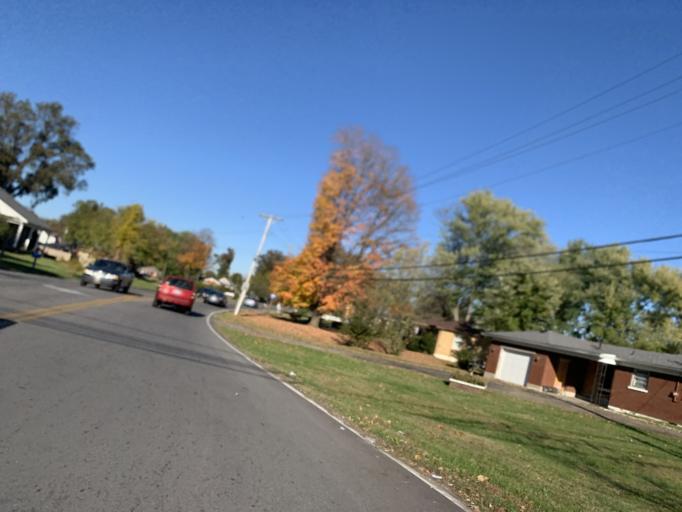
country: US
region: Kentucky
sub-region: Jefferson County
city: Pleasure Ridge Park
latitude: 38.1580
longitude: -85.8477
